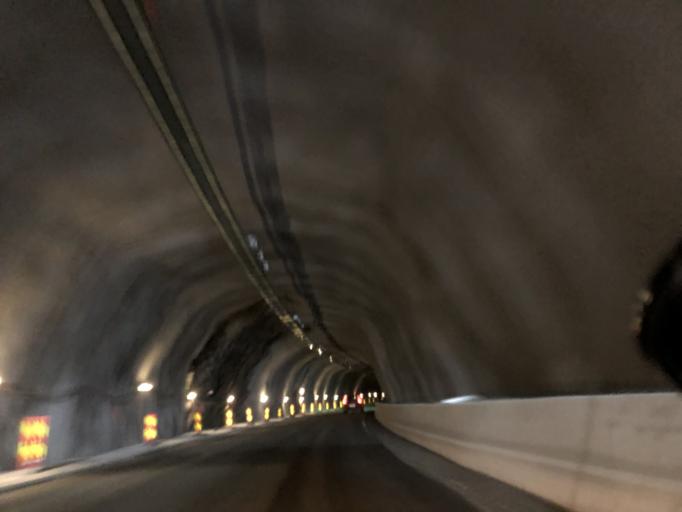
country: NO
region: Rogaland
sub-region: Bokn
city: Bokn
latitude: 59.2433
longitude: 5.4714
